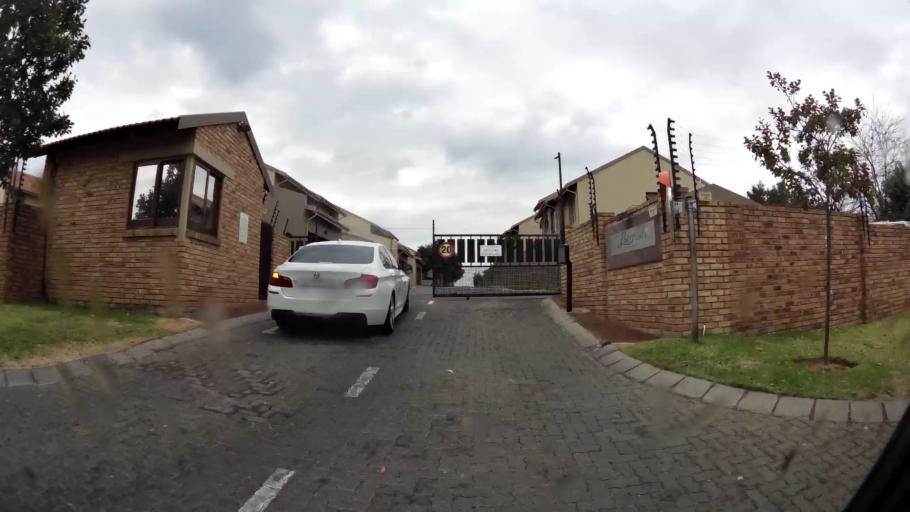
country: ZA
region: Gauteng
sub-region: City of Johannesburg Metropolitan Municipality
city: Roodepoort
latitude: -26.1142
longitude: 27.9142
